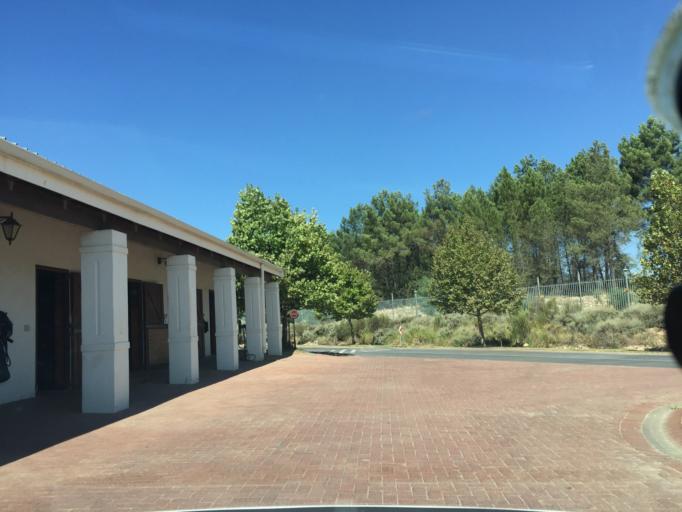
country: ZA
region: Western Cape
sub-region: Cape Winelands District Municipality
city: Paarl
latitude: -33.8064
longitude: 18.9689
